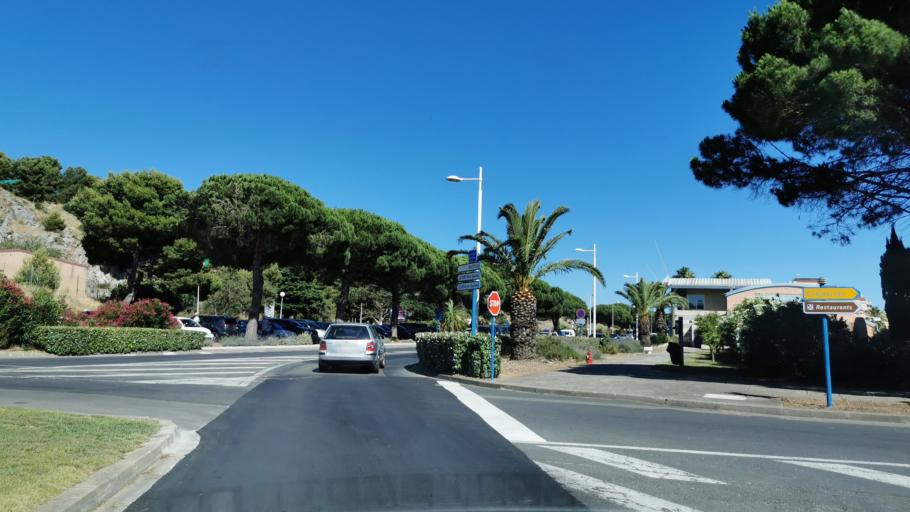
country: FR
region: Languedoc-Roussillon
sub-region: Departement de l'Aude
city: Gruissan
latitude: 43.1117
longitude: 3.0945
